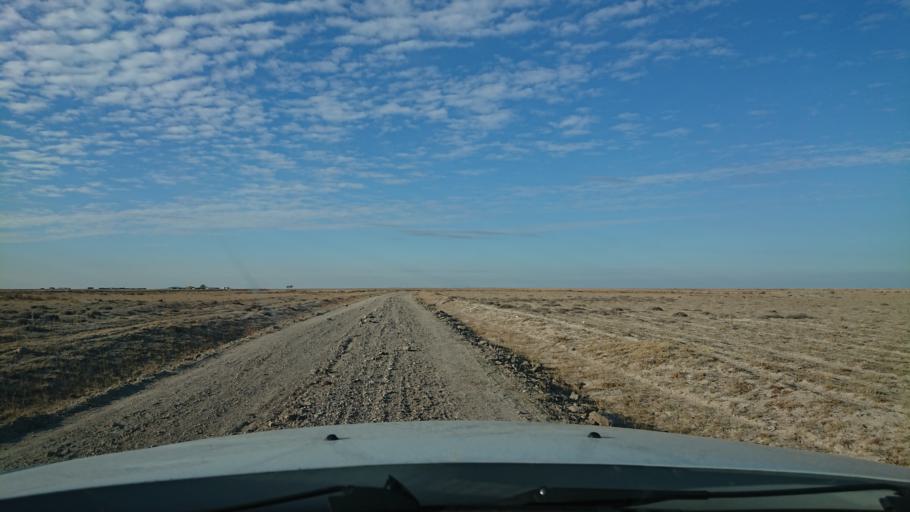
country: TR
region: Aksaray
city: Eskil
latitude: 38.5612
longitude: 33.3076
